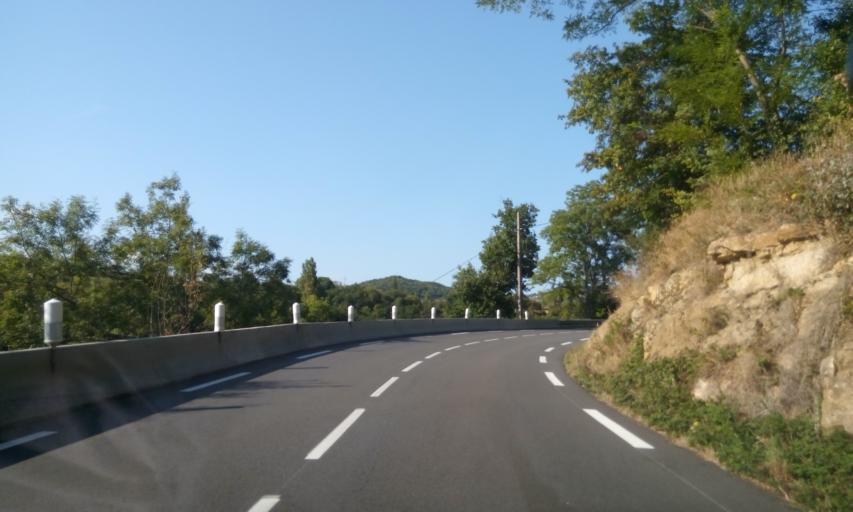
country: FR
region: Rhone-Alpes
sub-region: Departement du Rhone
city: Chatillon
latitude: 45.9115
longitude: 4.5927
